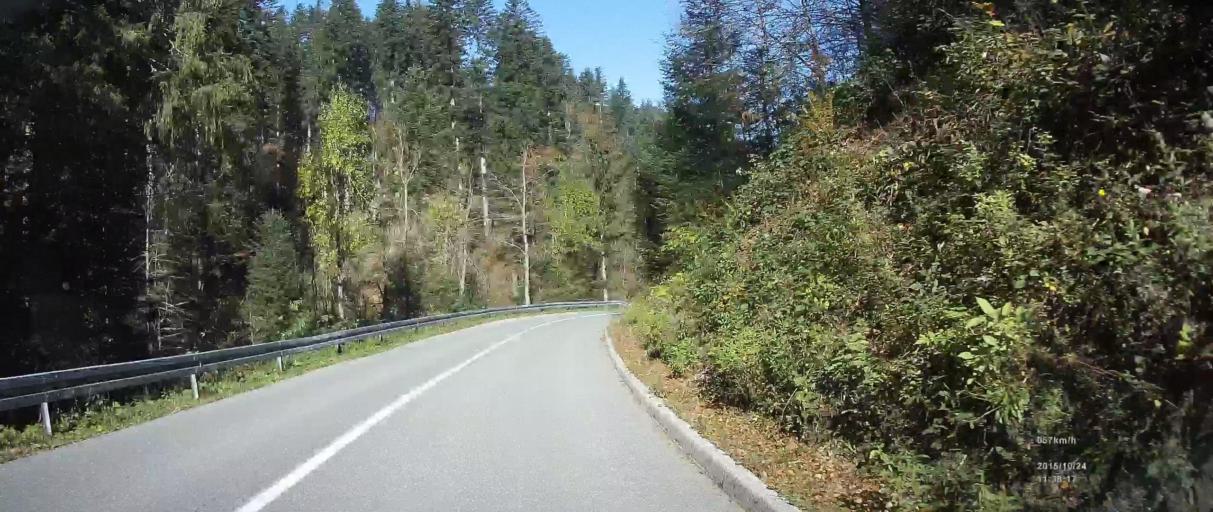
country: HR
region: Primorsko-Goranska
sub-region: Grad Delnice
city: Delnice
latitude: 45.4031
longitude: 14.7003
